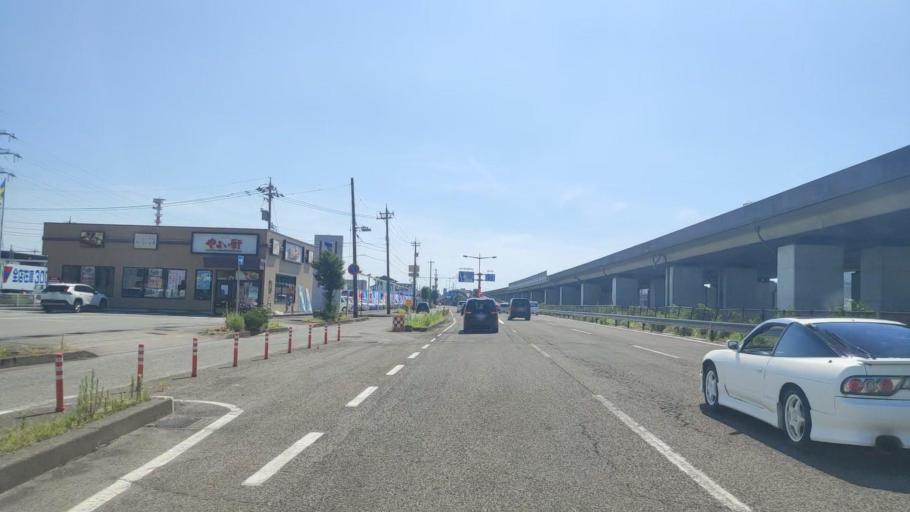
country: JP
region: Ishikawa
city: Kanazawa-shi
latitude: 36.5936
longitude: 136.6349
